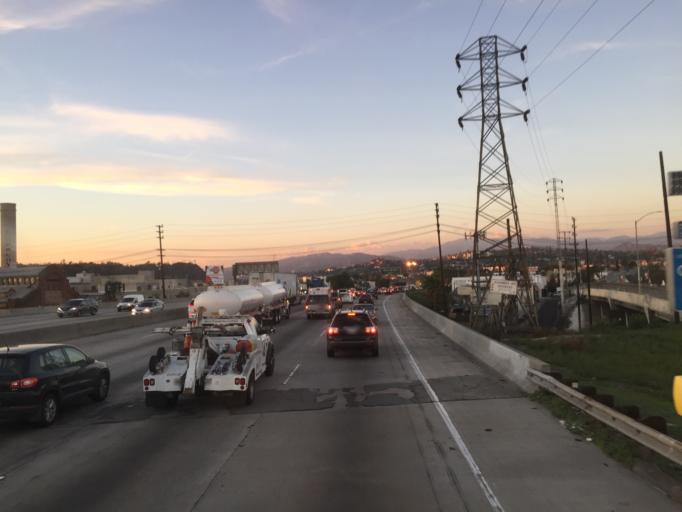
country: US
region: California
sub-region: Los Angeles County
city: Los Angeles
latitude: 34.0624
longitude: -118.2156
